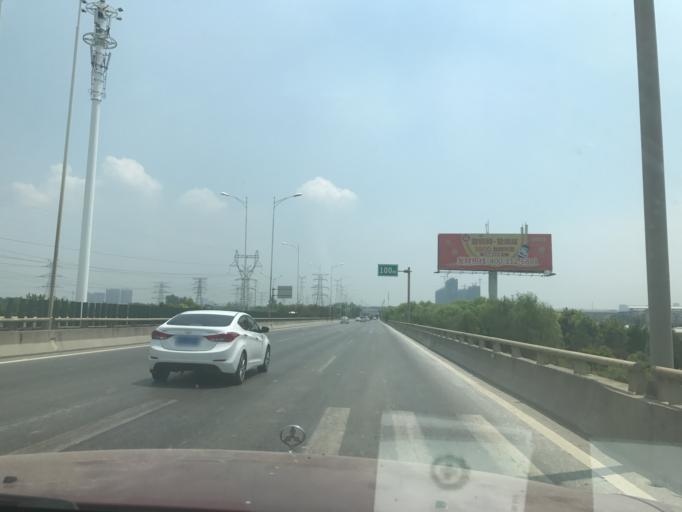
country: CN
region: Hubei
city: Houhu
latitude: 30.6865
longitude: 114.3284
